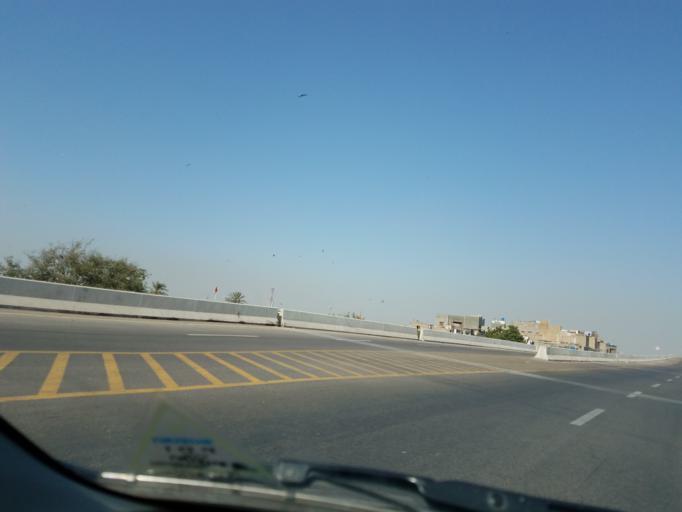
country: PK
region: Sindh
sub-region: Karachi District
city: Karachi
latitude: 24.8830
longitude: 67.0189
